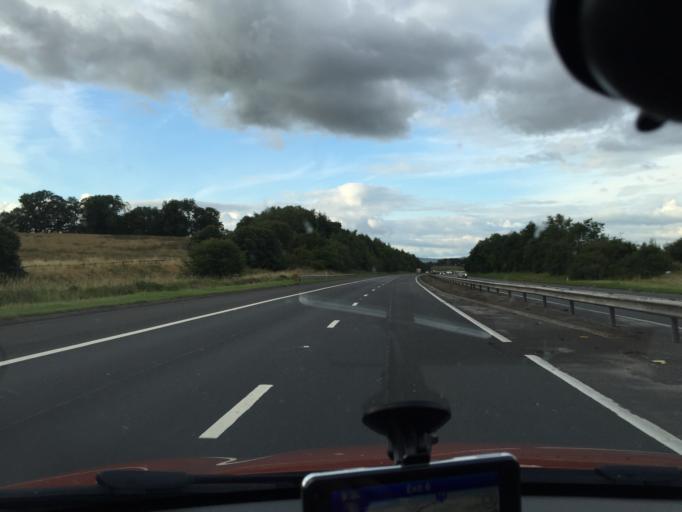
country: GB
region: Scotland
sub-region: North Lanarkshire
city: Glenboig
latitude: 55.9049
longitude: -4.0678
